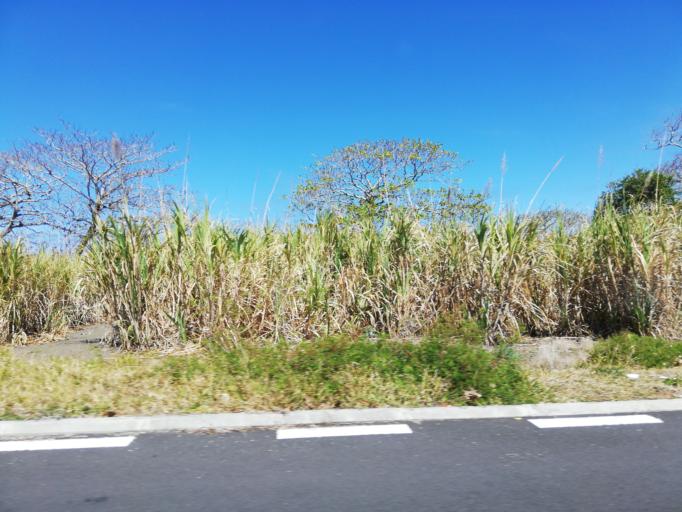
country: MU
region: Grand Port
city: Beau Vallon
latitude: -20.4523
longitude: 57.6957
